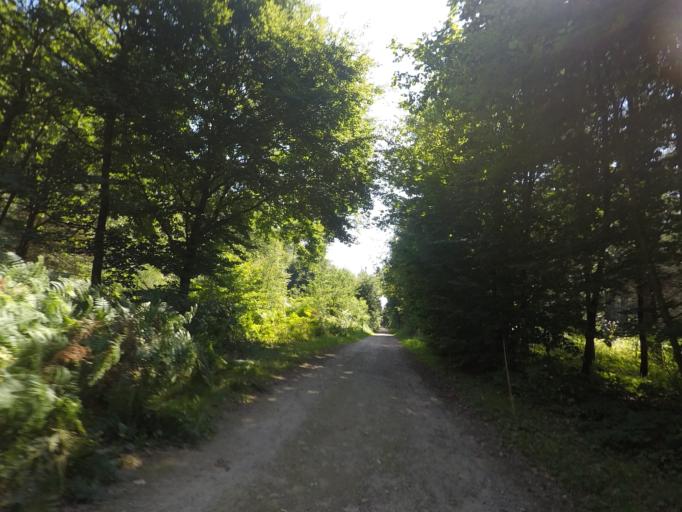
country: LU
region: Luxembourg
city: Bereldange
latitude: 49.6422
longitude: 6.1094
